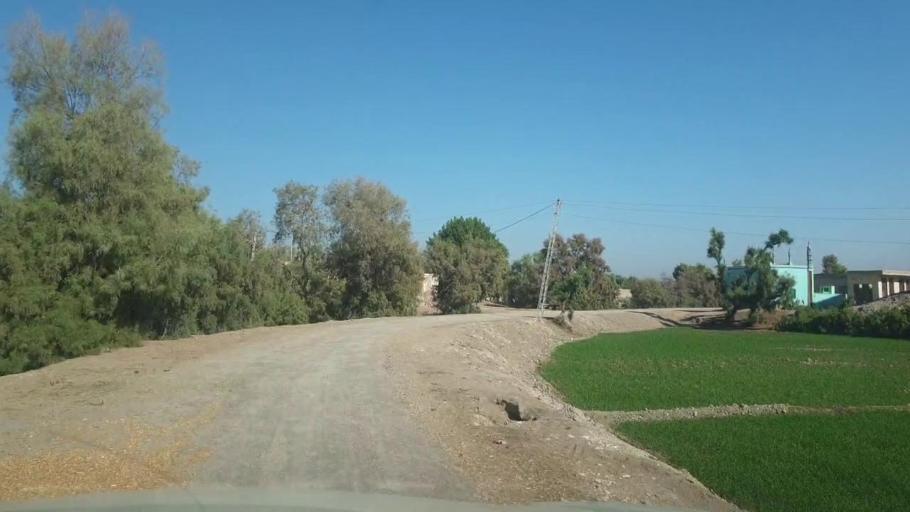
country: PK
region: Sindh
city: Bhan
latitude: 26.5249
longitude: 67.6423
